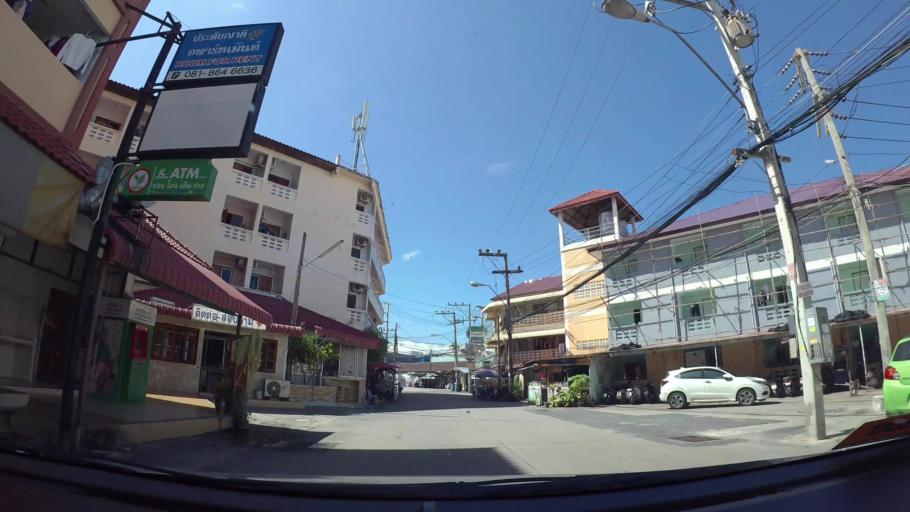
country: TH
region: Chon Buri
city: Phatthaya
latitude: 12.9299
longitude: 100.8973
